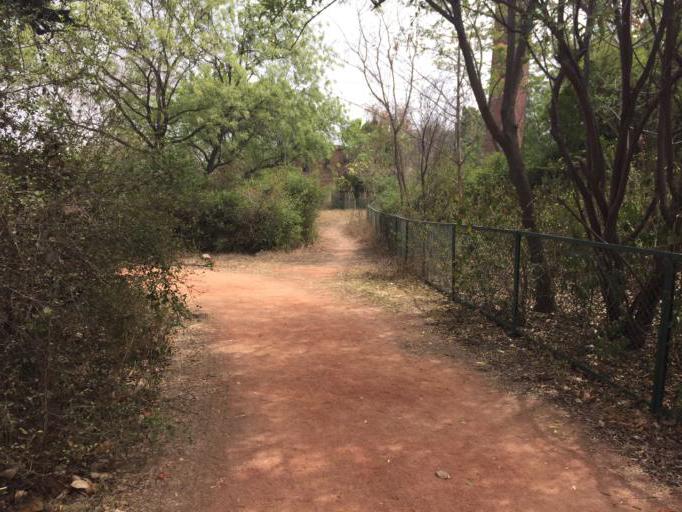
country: IN
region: NCT
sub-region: Central Delhi
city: Karol Bagh
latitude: 28.5571
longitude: 77.1465
